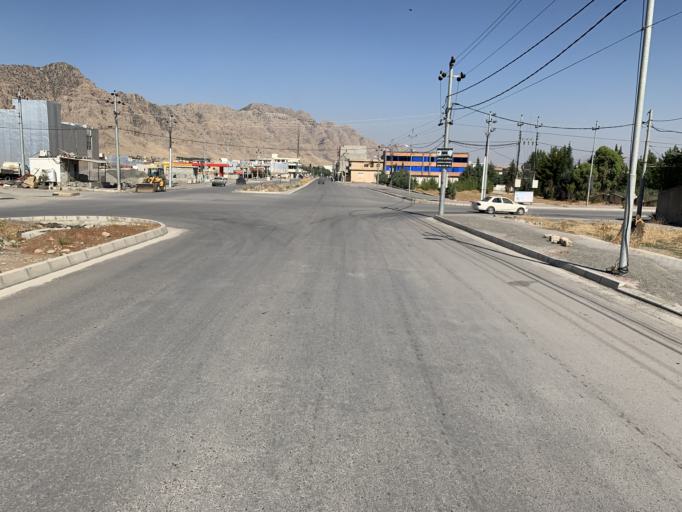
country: IQ
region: As Sulaymaniyah
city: Raniye
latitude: 36.2577
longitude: 44.8717
